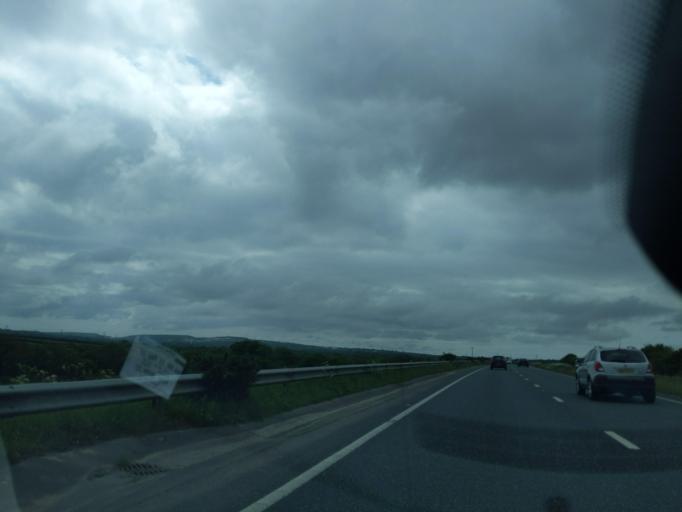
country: GB
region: England
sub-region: Cornwall
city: Roche
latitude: 50.4183
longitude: -4.8605
